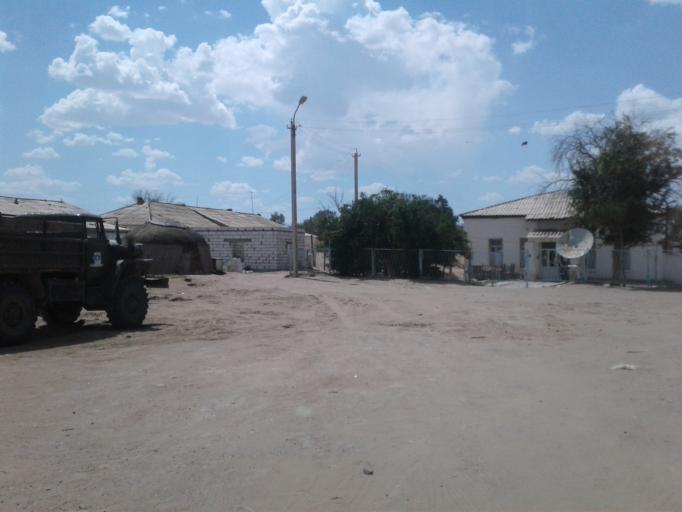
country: TM
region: Ahal
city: Abadan
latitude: 38.7660
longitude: 58.4934
